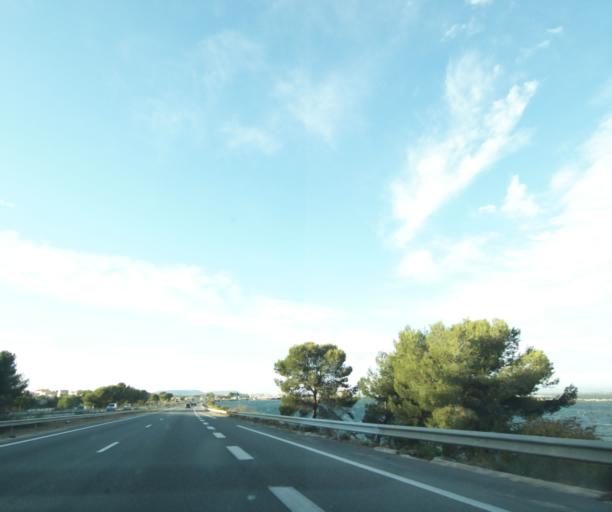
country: FR
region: Provence-Alpes-Cote d'Azur
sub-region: Departement des Bouches-du-Rhone
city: Chateauneuf-les-Martigues
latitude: 43.3971
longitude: 5.1230
